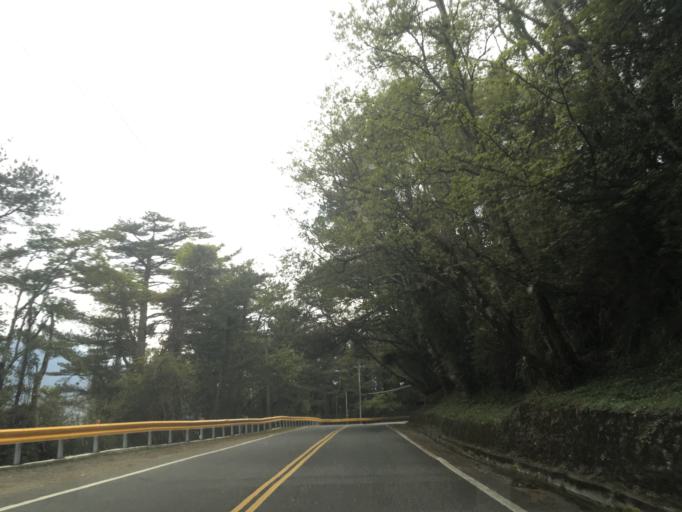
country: TW
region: Taiwan
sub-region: Hualien
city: Hualian
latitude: 24.1835
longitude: 121.3268
